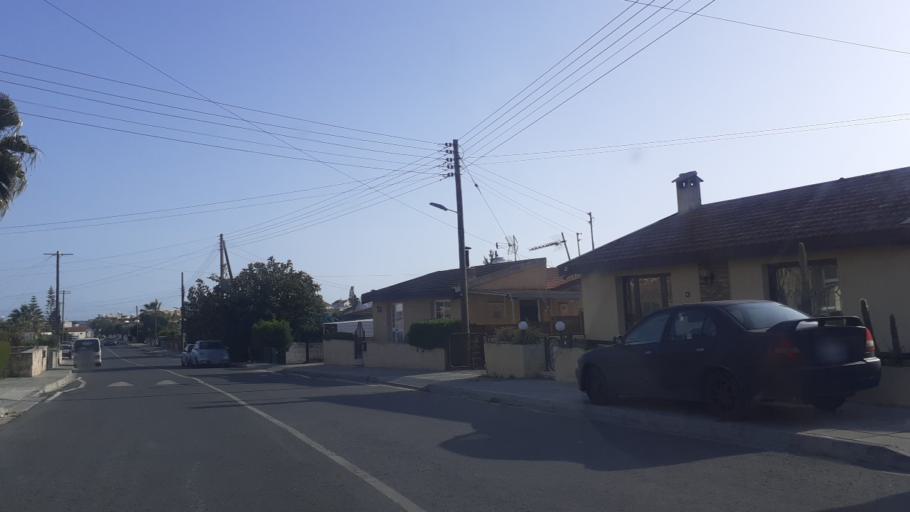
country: CY
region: Larnaka
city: Kolossi
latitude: 34.6601
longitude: 32.9564
